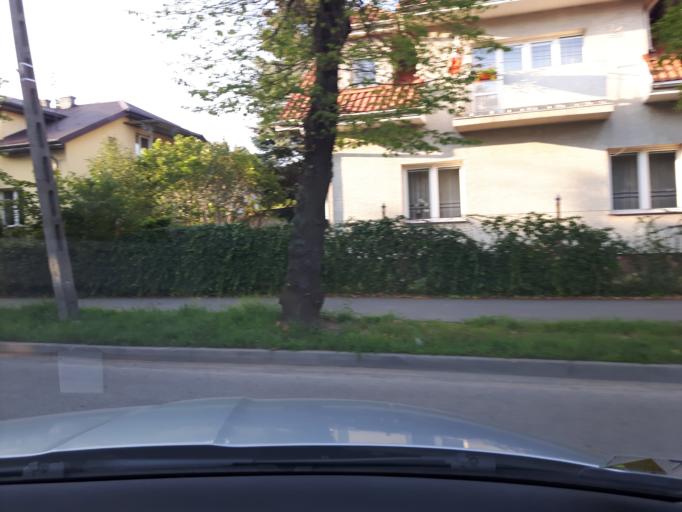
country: PL
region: Masovian Voivodeship
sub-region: Powiat wolominski
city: Marki
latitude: 52.3172
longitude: 21.1026
